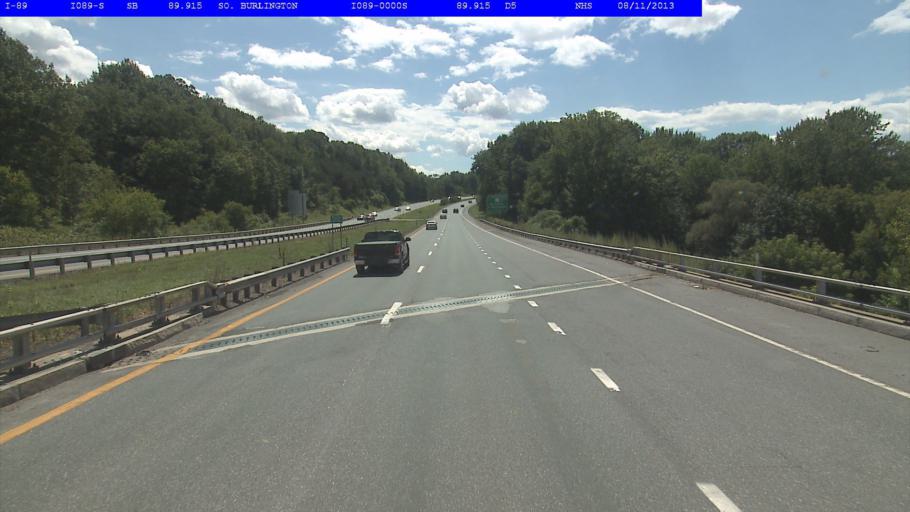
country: US
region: Vermont
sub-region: Chittenden County
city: Winooski
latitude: 44.4851
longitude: -73.1740
